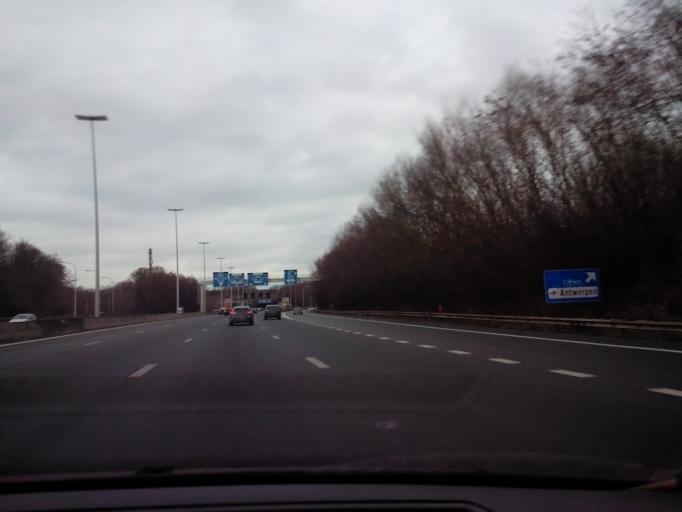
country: BE
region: Flanders
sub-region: Provincie Antwerpen
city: Edegem
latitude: 51.1668
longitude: 4.4137
